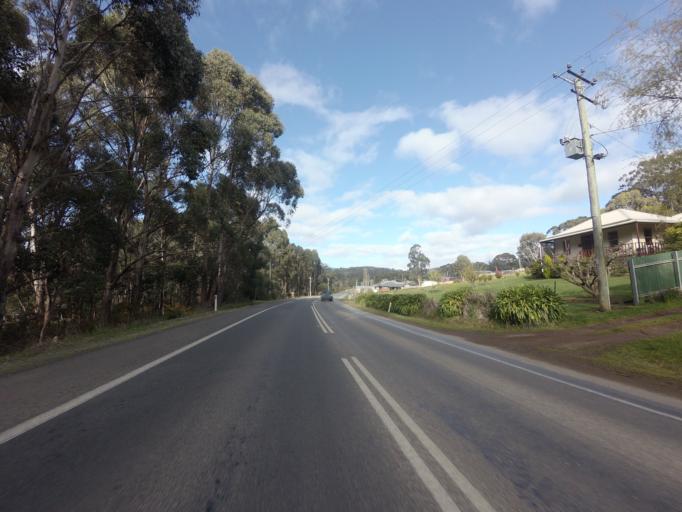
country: AU
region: Tasmania
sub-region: Huon Valley
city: Geeveston
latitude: -43.1629
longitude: 146.9497
